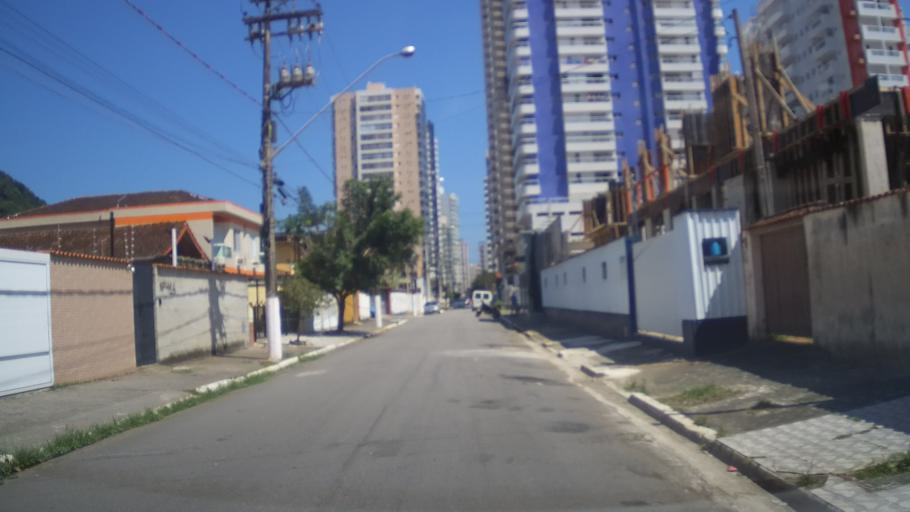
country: BR
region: Sao Paulo
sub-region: Praia Grande
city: Praia Grande
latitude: -24.0120
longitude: -46.3967
